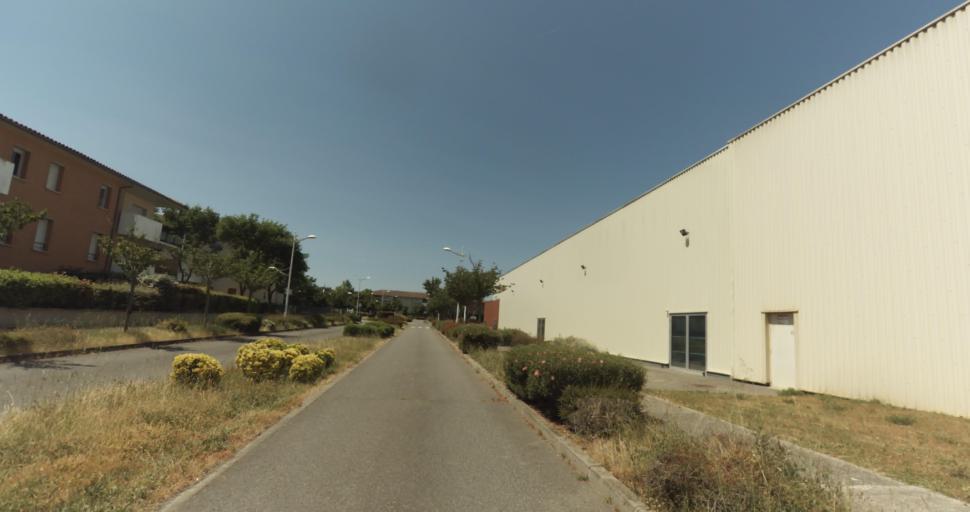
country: FR
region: Midi-Pyrenees
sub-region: Departement de la Haute-Garonne
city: La Salvetat-Saint-Gilles
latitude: 43.6004
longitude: 1.2639
